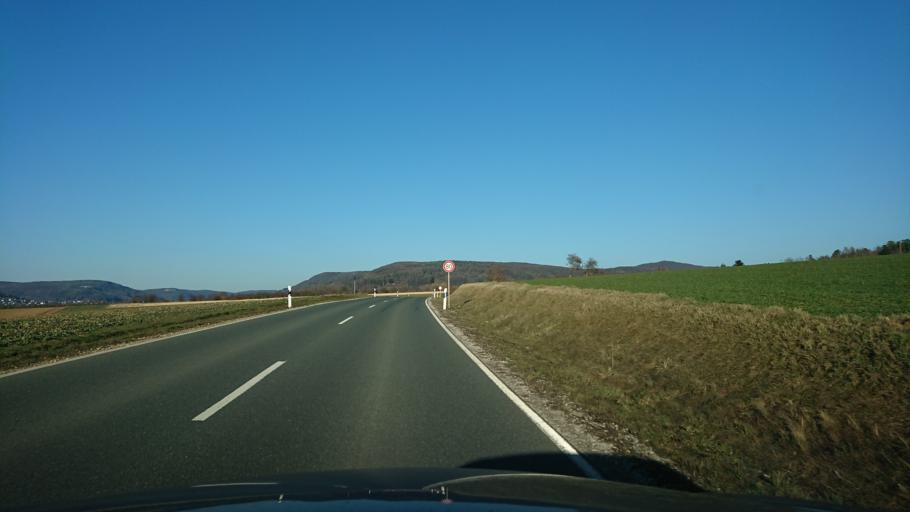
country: DE
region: Bavaria
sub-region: Upper Franconia
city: Kirchehrenbach
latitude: 49.7443
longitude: 11.1608
